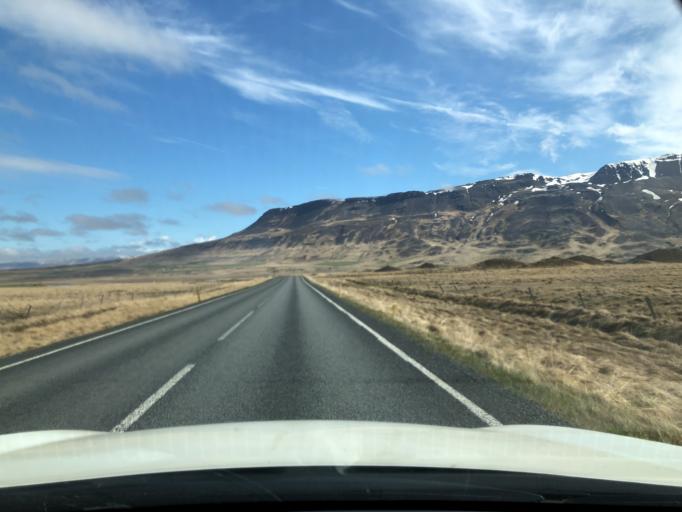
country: IS
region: Northwest
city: Saudarkrokur
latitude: 65.5020
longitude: -20.3948
